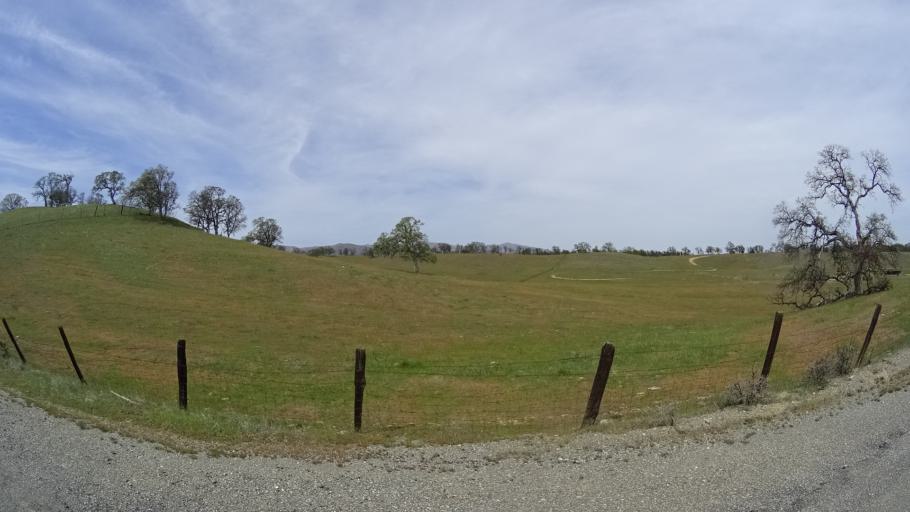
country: US
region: California
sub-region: Glenn County
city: Willows
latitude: 39.5946
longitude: -122.5531
